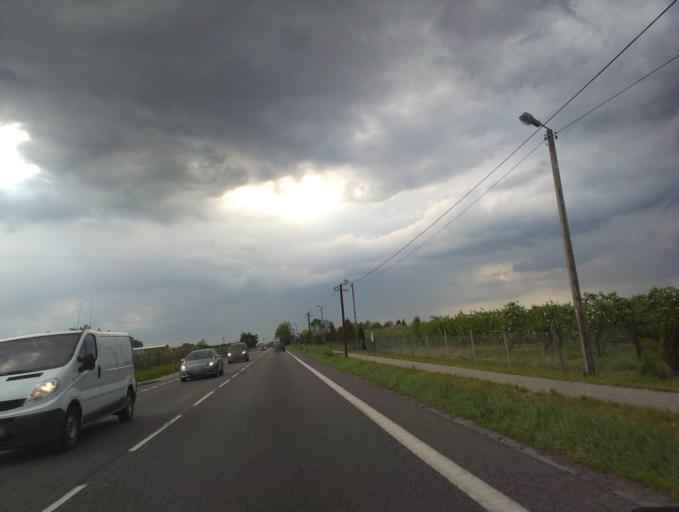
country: PL
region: Masovian Voivodeship
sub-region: Powiat grojecki
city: Pniewy
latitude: 51.9121
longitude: 20.7265
